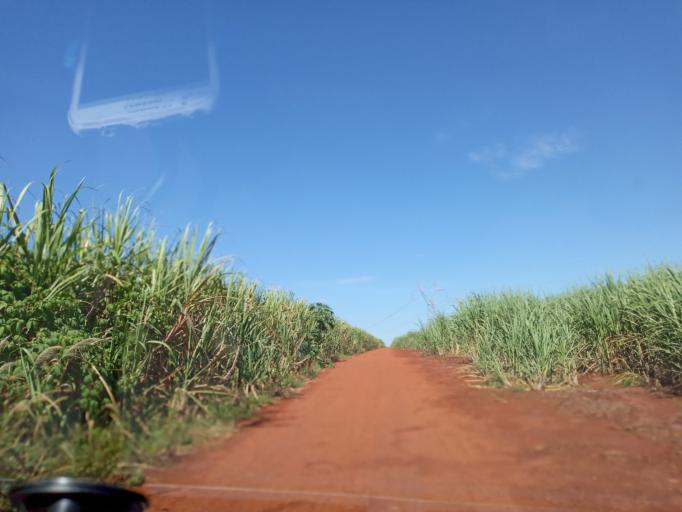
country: BR
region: Goias
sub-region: Itumbiara
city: Itumbiara
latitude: -18.4523
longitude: -49.1441
